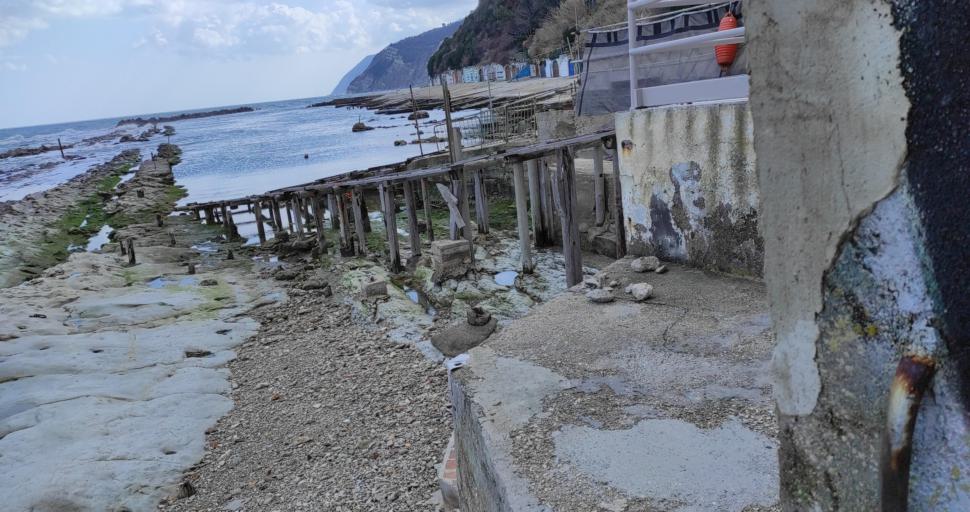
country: IT
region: The Marches
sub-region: Provincia di Ancona
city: Pietra la Croce
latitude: 43.6190
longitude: 13.5315
